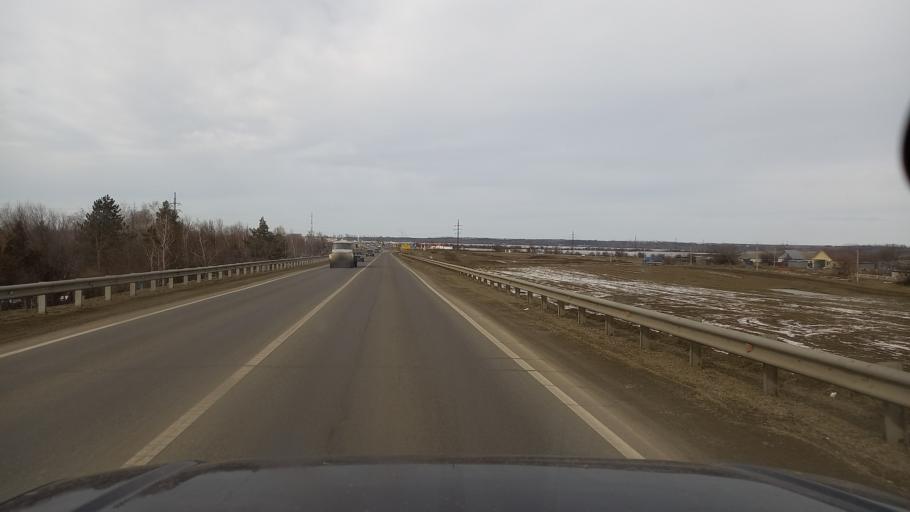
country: RU
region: Krasnodarskiy
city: Belorechensk
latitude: 44.7643
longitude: 39.9136
